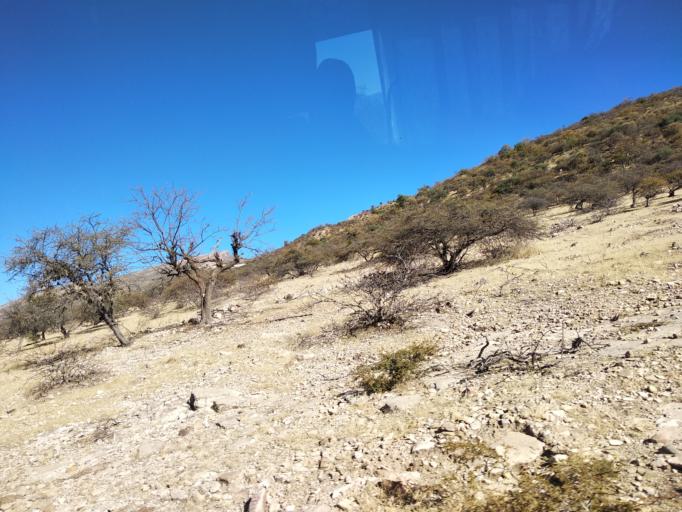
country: BO
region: Cochabamba
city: Mizque
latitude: -18.0832
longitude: -65.7488
